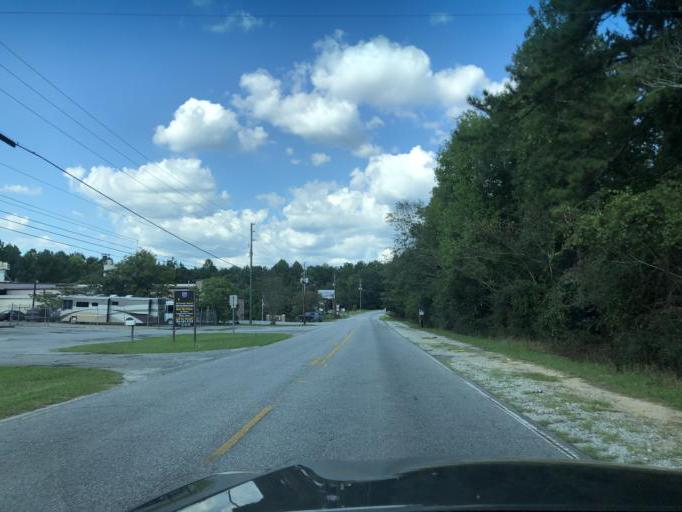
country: US
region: Georgia
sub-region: Muscogee County
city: Columbus
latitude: 32.5176
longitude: -84.9100
